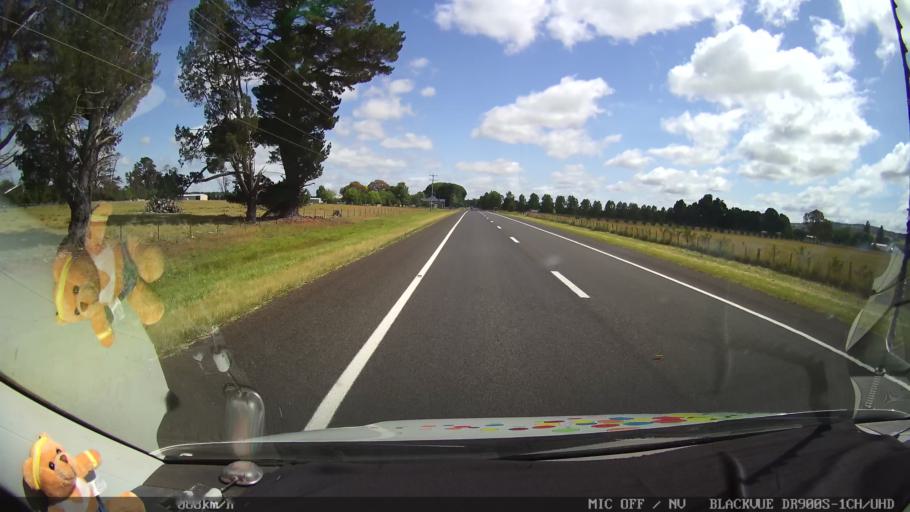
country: AU
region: New South Wales
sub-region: Glen Innes Severn
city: Glen Innes
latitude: -29.8200
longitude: 151.7403
